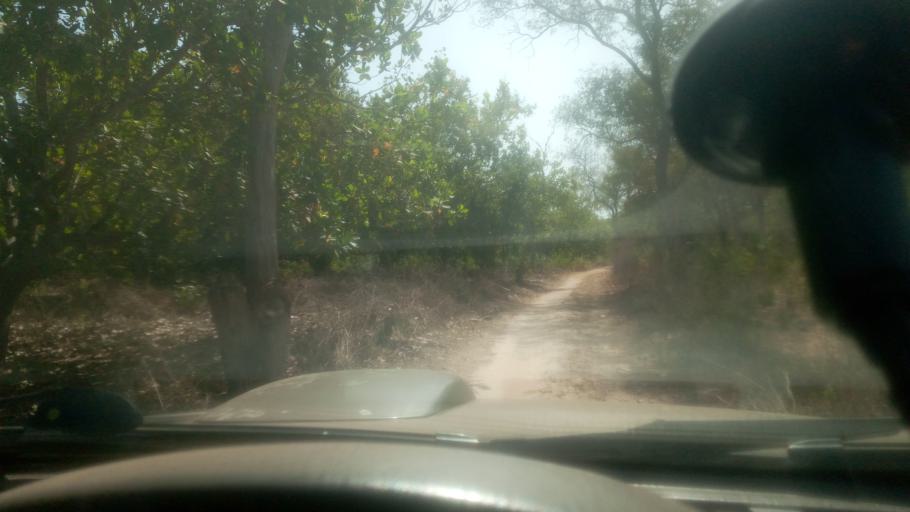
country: GW
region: Oio
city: Farim
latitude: 12.4541
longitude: -15.4113
